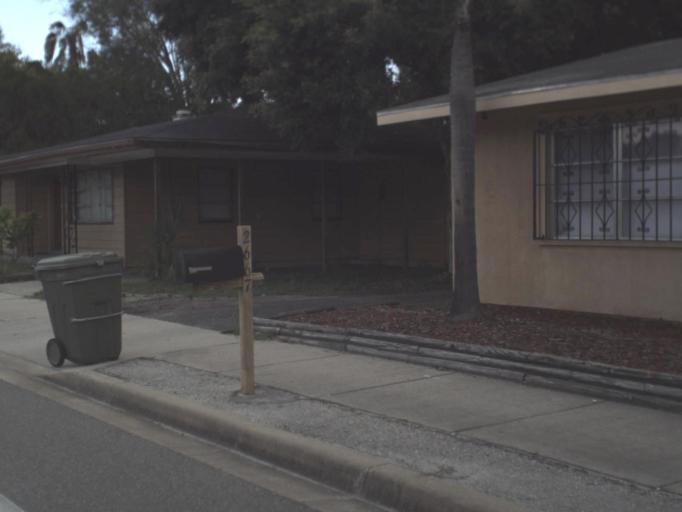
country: US
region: Florida
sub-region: Sarasota County
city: Sarasota
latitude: 27.3377
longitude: -82.5167
